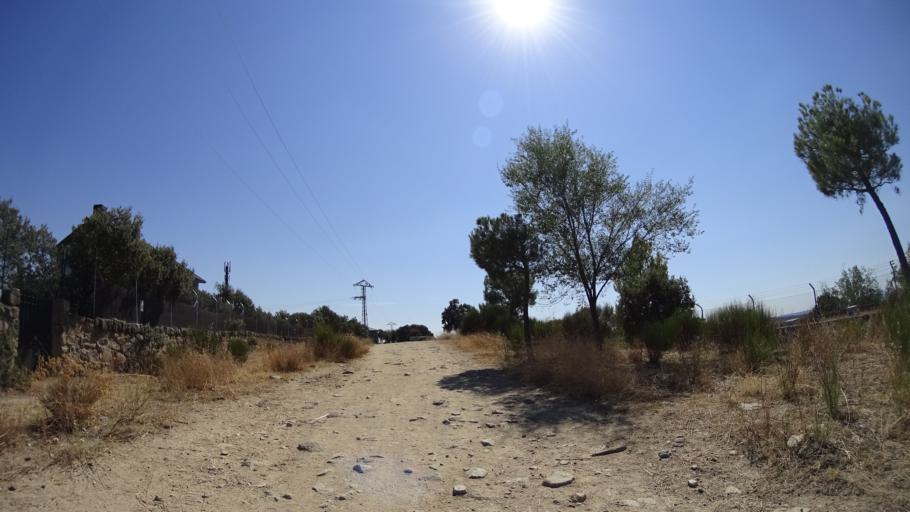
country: ES
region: Madrid
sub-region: Provincia de Madrid
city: Galapagar
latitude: 40.6055
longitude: -4.0114
